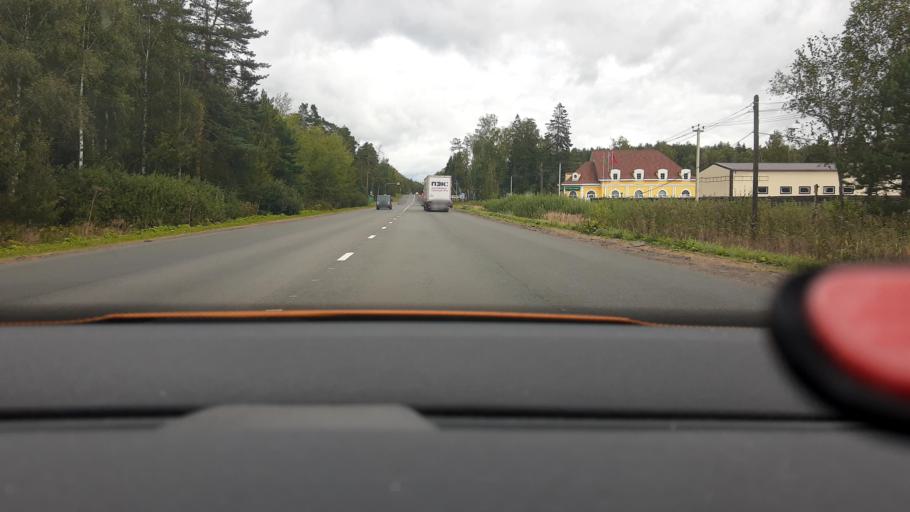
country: RU
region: Moskovskaya
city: Lesnoy
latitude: 56.0558
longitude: 38.0016
